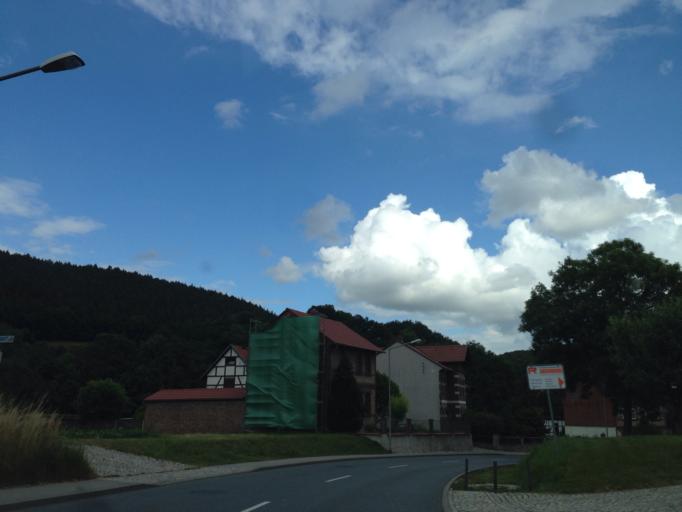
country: DE
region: Thuringia
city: Rudolstadt
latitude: 50.7364
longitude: 11.3306
